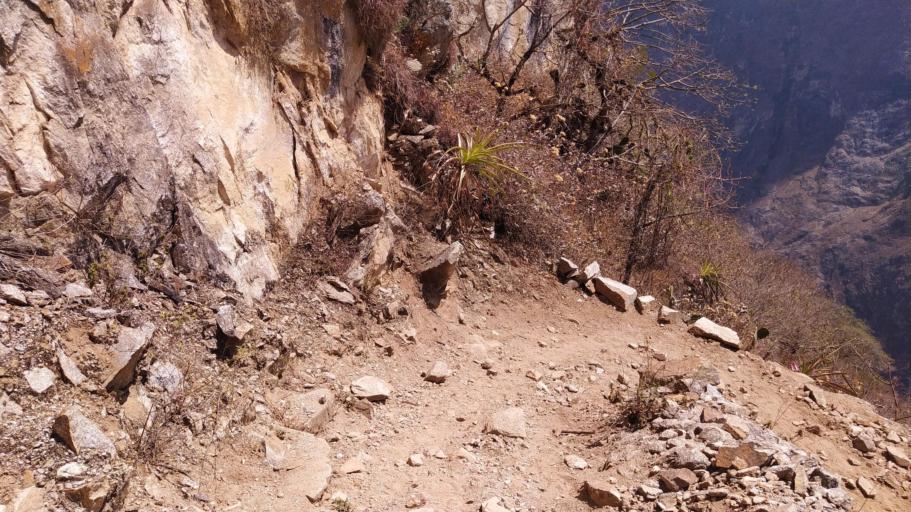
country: PE
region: Apurimac
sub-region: Provincia de Abancay
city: Cachora
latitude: -13.4335
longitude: -72.8245
